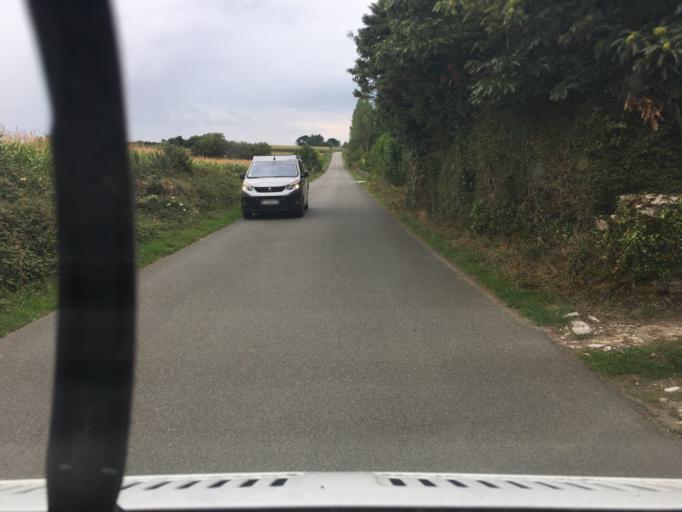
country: FR
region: Brittany
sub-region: Departement du Finistere
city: Beuzec-Cap-Sizun
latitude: 48.0737
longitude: -4.4750
